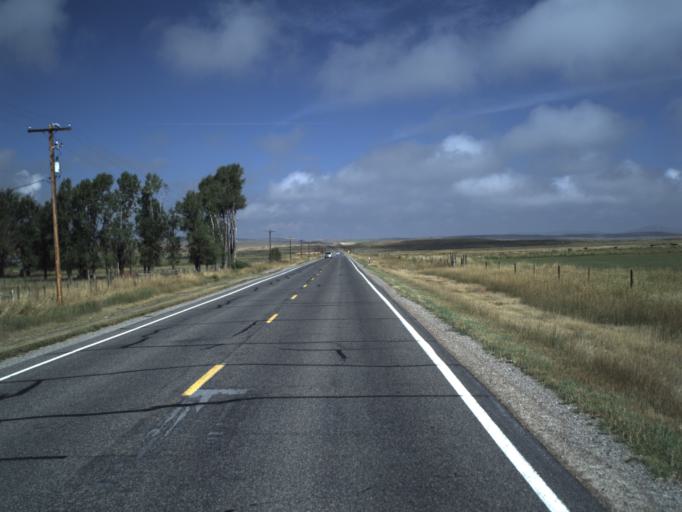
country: US
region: Utah
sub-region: Rich County
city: Randolph
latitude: 41.7161
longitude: -111.1593
